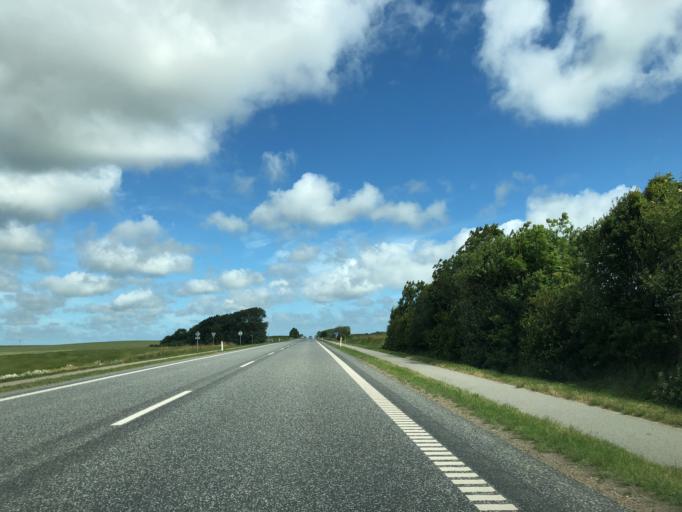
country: DK
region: Central Jutland
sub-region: Holstebro Kommune
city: Holstebro
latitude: 56.4193
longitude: 8.6016
